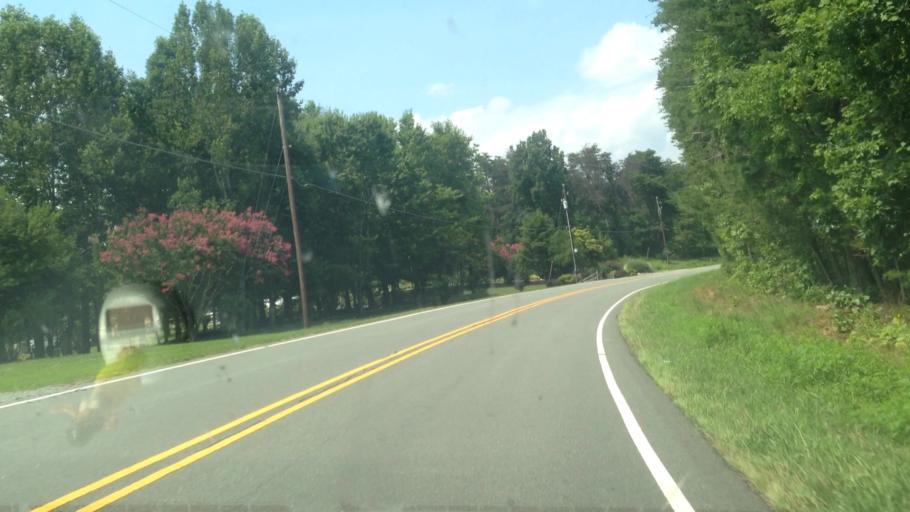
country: US
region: North Carolina
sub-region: Stokes County
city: Danbury
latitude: 36.3988
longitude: -80.0951
